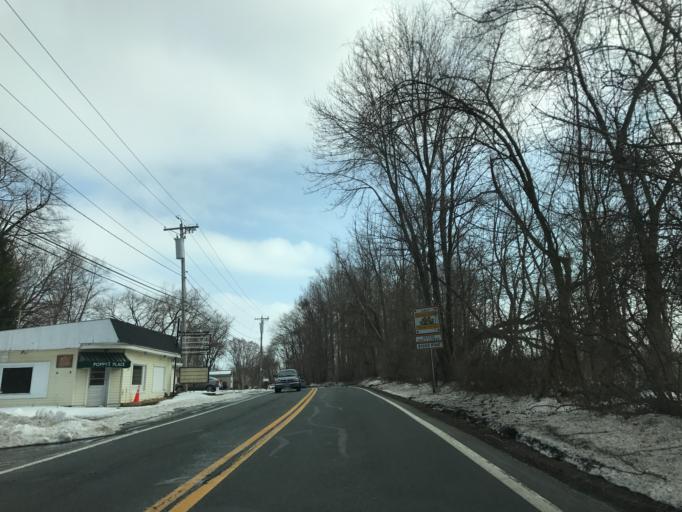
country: US
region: Maryland
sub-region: Harford County
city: South Bel Air
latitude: 39.6352
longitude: -76.2673
